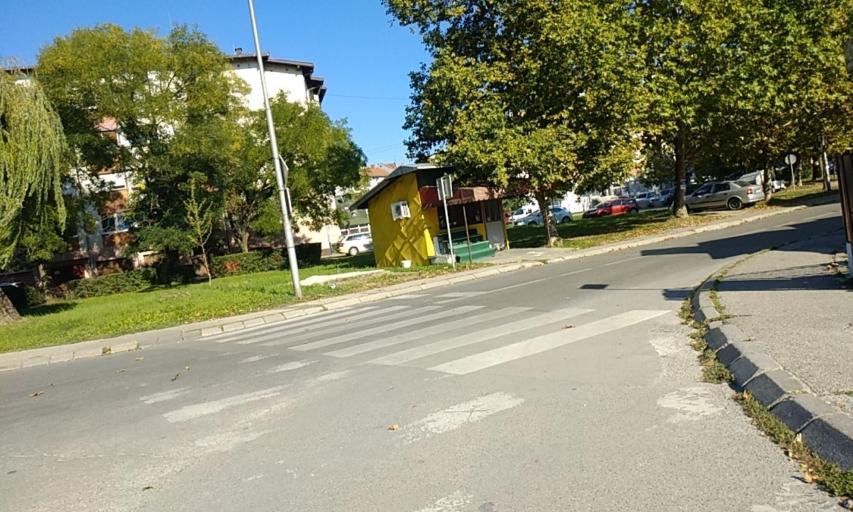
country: BA
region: Republika Srpska
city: Mejdan - Obilicevo
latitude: 44.7601
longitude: 17.1994
